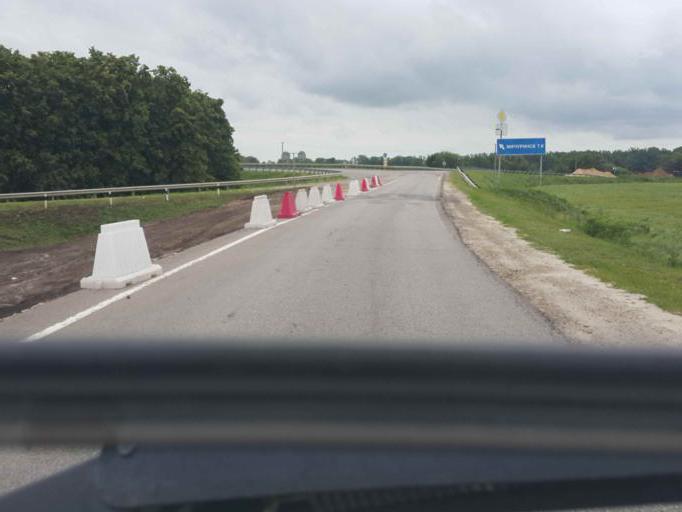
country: RU
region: Tambov
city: Zavoronezhskoye
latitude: 52.9090
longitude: 40.6365
